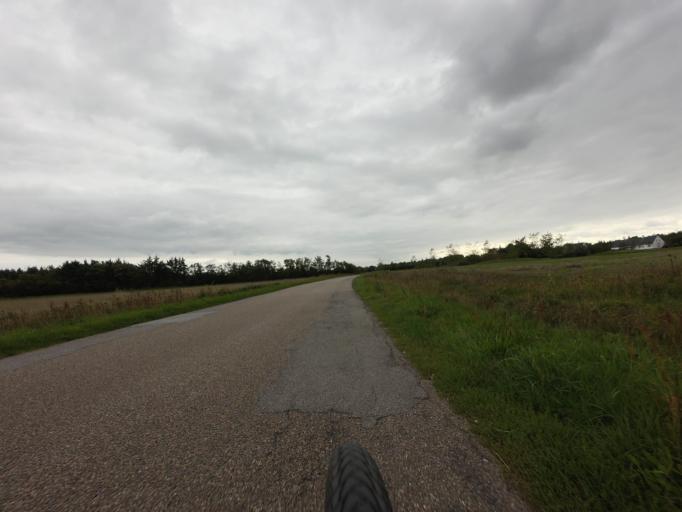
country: DK
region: North Denmark
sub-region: Hjorring Kommune
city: Hirtshals
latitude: 57.5685
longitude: 10.0329
